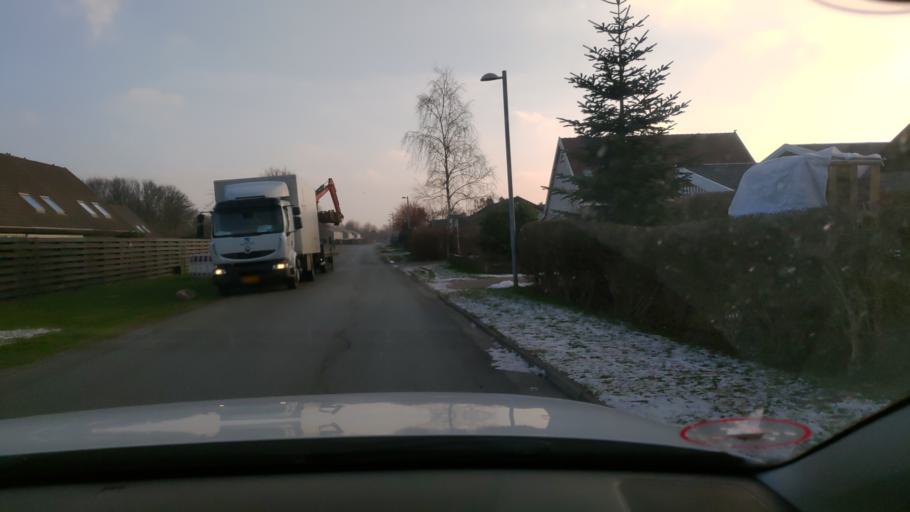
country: DK
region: Zealand
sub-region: Solrod Kommune
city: Solrod Strand
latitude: 55.5432
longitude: 12.2208
